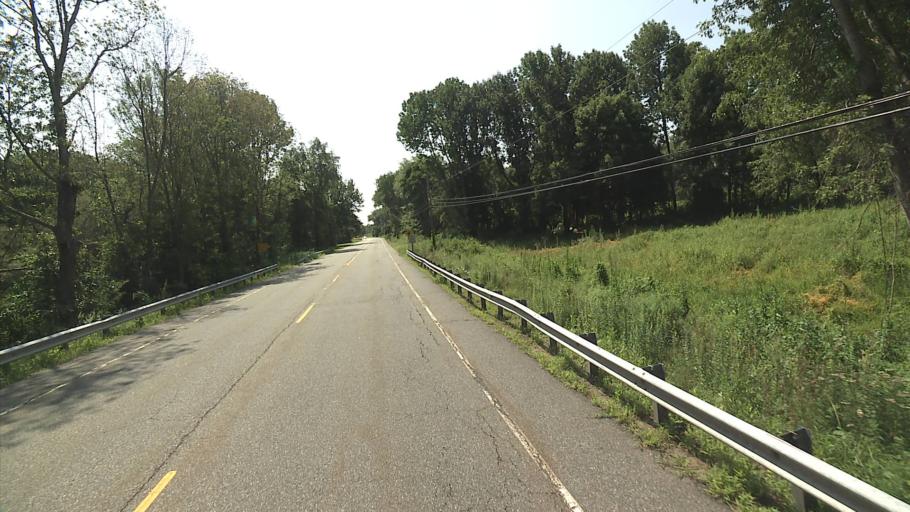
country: US
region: Connecticut
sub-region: New London County
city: Colchester
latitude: 41.5194
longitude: -72.2558
